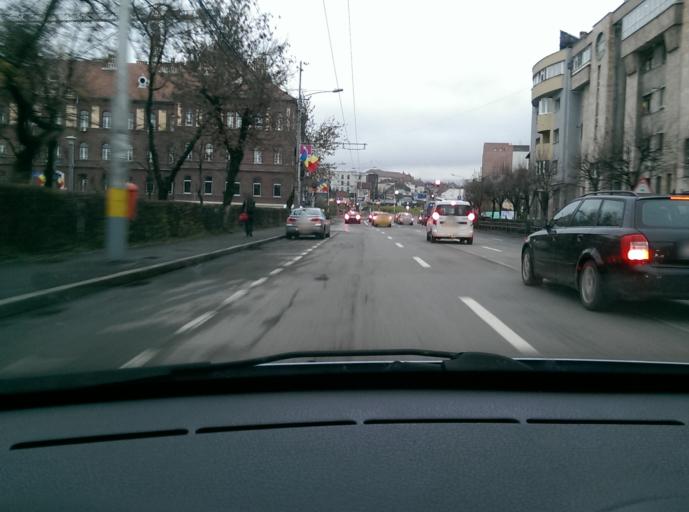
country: RO
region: Cluj
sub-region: Municipiul Cluj-Napoca
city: Cluj-Napoca
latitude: 46.7694
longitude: 23.5974
